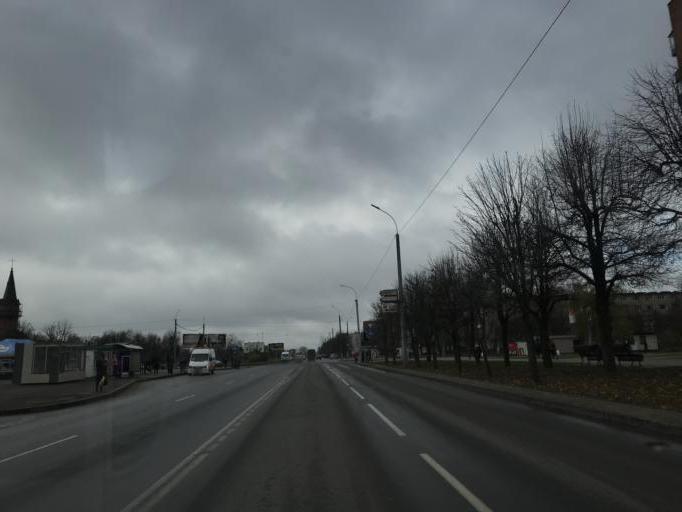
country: BY
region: Mogilev
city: Mahilyow
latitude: 53.8713
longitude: 30.3251
